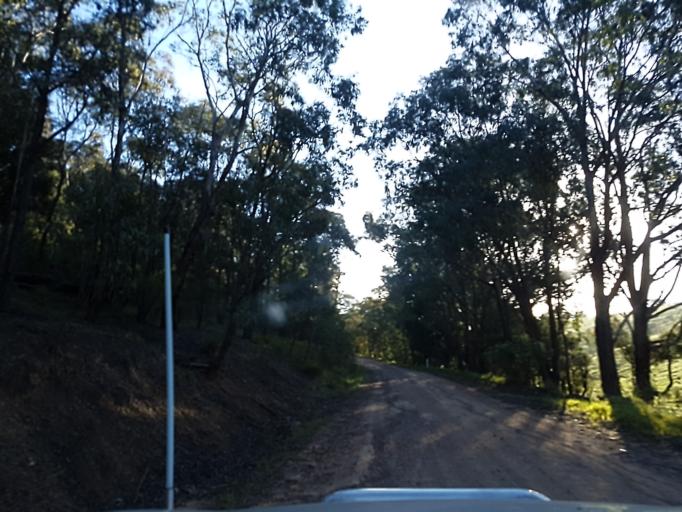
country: AU
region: Victoria
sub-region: East Gippsland
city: Bairnsdale
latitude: -37.4841
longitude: 147.2018
